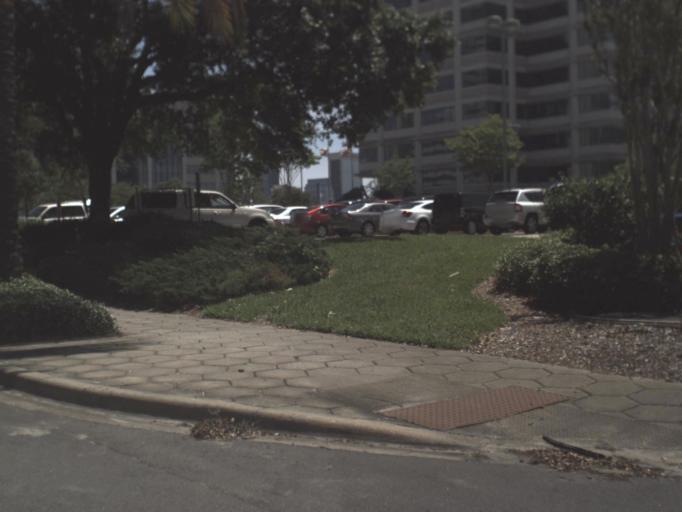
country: US
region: Florida
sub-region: Duval County
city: Jacksonville
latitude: 30.3177
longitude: -81.6759
